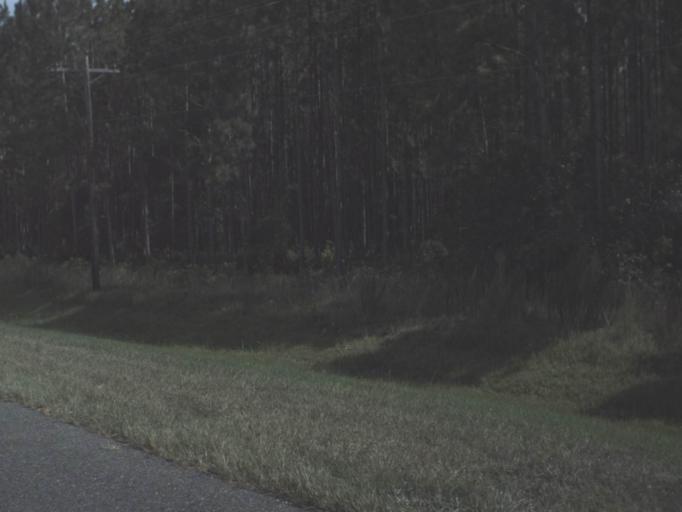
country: US
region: Florida
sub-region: Levy County
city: Chiefland
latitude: 29.3984
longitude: -82.8121
